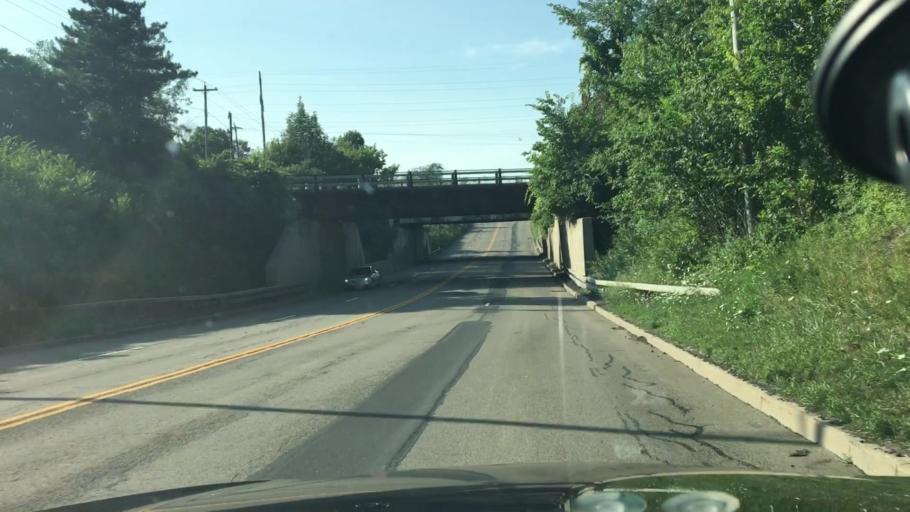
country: US
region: New York
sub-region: Erie County
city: Wanakah
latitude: 42.7642
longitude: -78.8640
